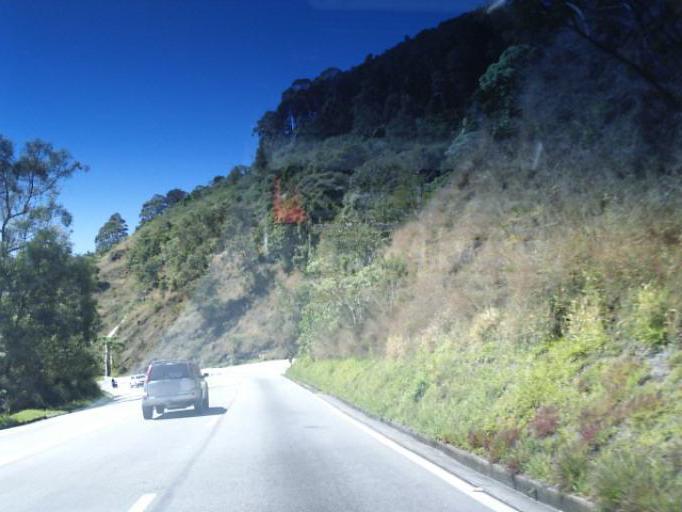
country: BR
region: Sao Paulo
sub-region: Campos Do Jordao
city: Campos do Jordao
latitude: -22.7918
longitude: -45.6218
